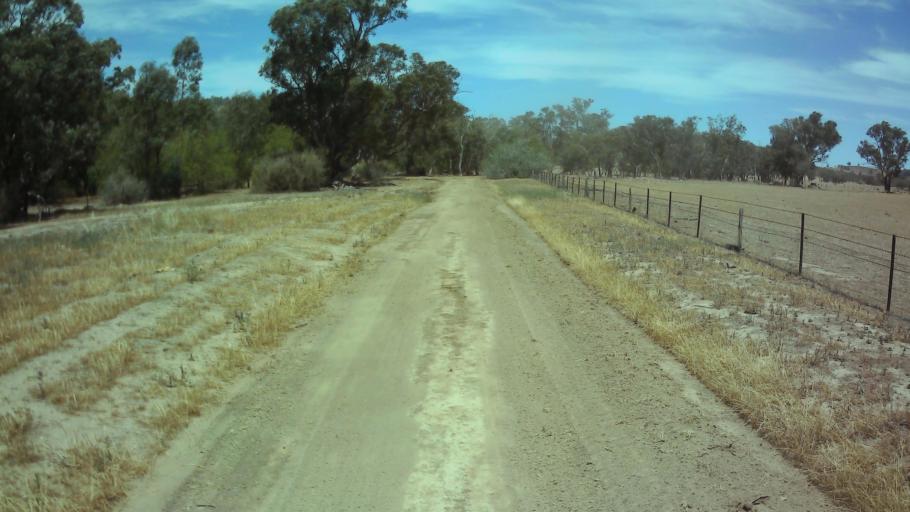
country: AU
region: New South Wales
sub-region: Weddin
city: Grenfell
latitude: -33.7661
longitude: 148.1492
